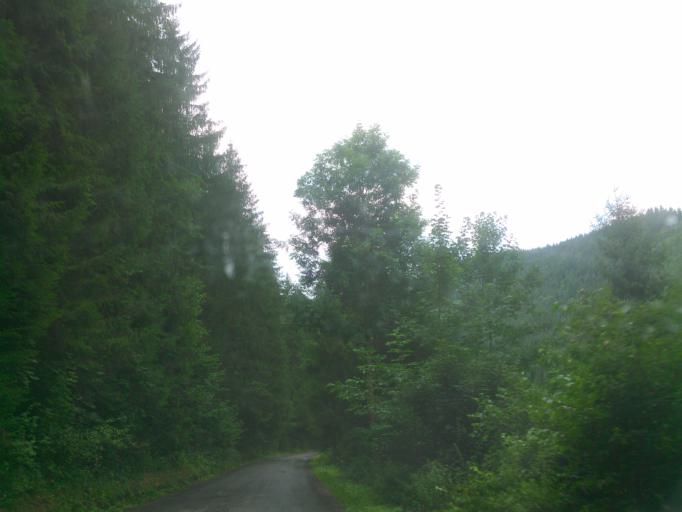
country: SK
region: Zilinsky
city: Ruzomberok
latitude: 49.0426
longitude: 19.4204
